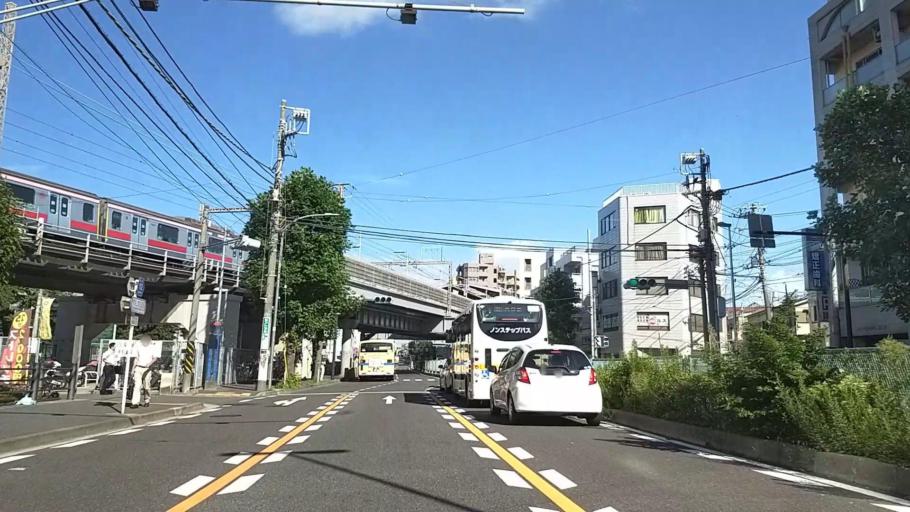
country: JP
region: Kanagawa
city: Yokohama
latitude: 35.4820
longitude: 139.6303
